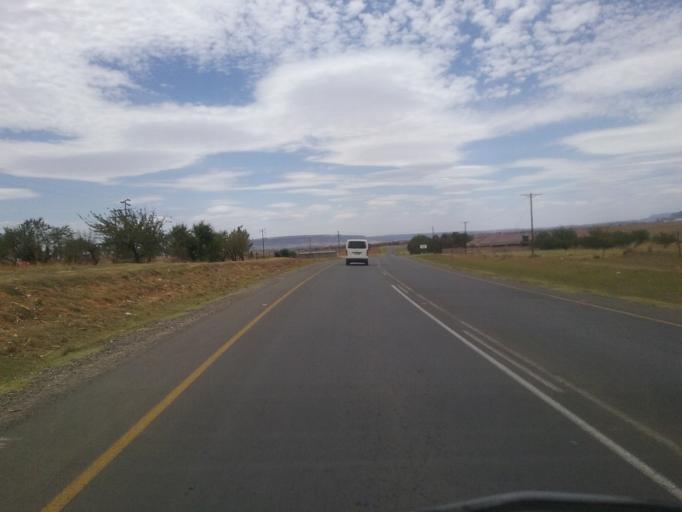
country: LS
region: Maseru
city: Maseru
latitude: -29.4818
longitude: 27.5270
